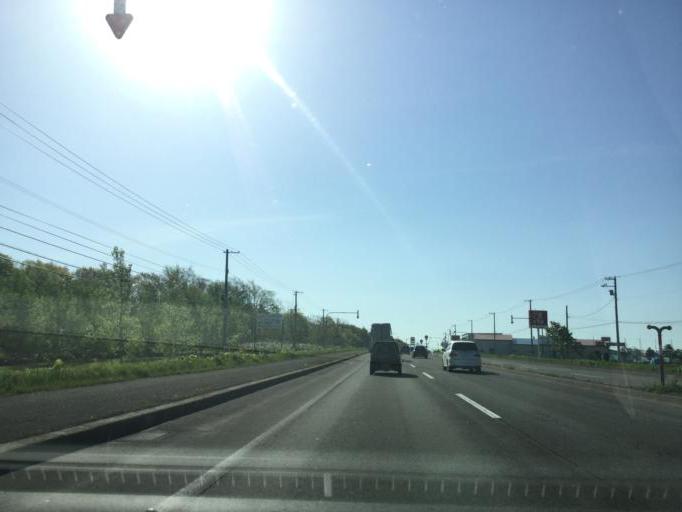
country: JP
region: Hokkaido
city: Kitahiroshima
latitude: 43.0093
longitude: 141.5167
